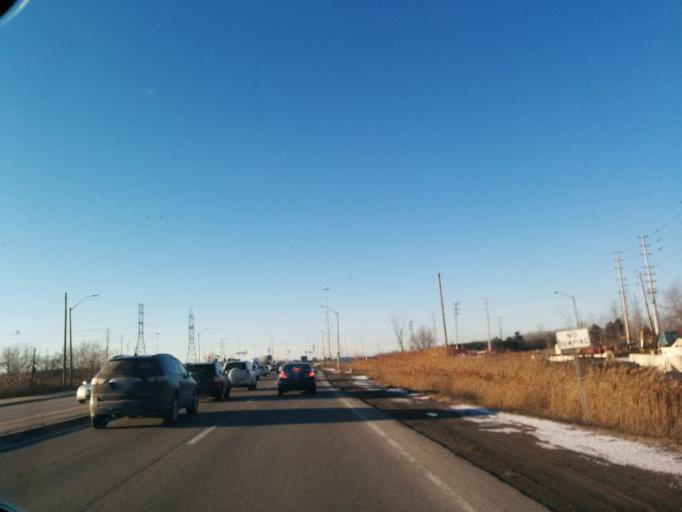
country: CA
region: Ontario
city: Mississauga
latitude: 43.6142
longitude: -79.6265
